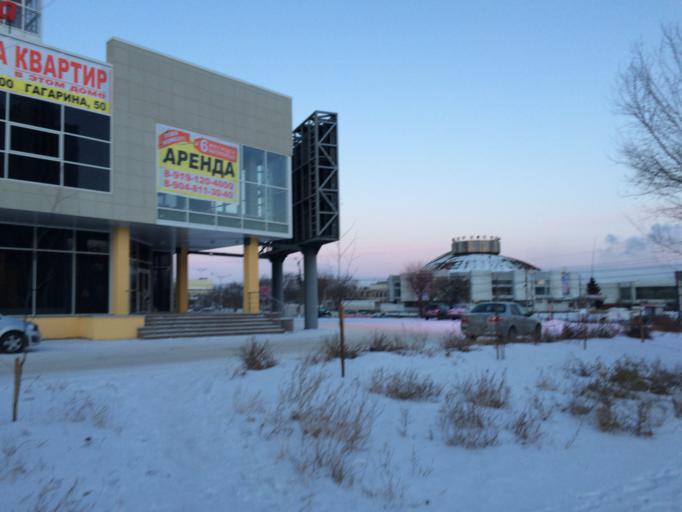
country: RU
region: Chelyabinsk
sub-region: Gorod Magnitogorsk
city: Magnitogorsk
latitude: 53.3983
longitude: 58.9846
